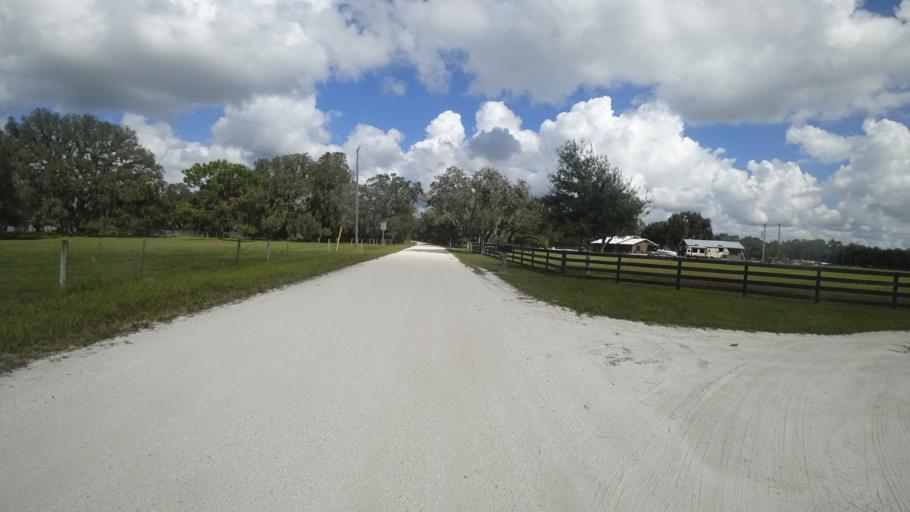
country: US
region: Florida
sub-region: Sarasota County
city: Lake Sarasota
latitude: 27.3852
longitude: -82.2192
